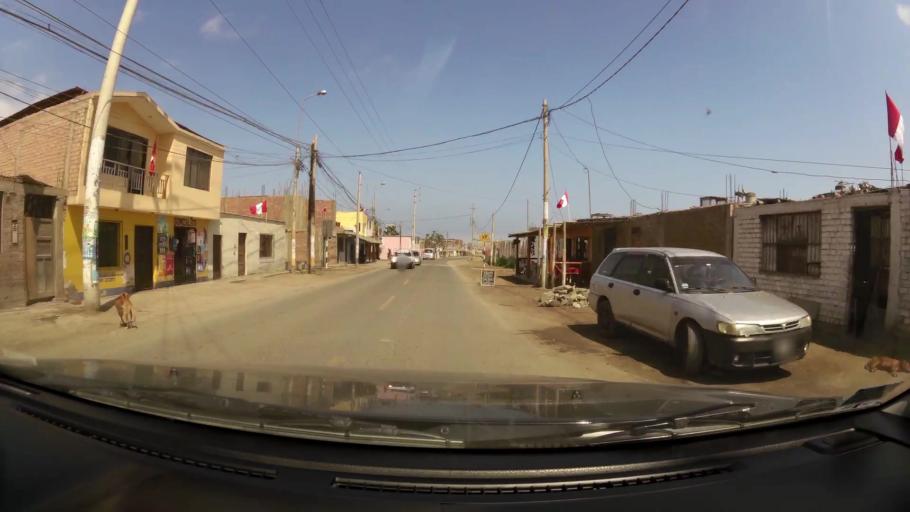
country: PE
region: Lima
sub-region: Provincia de Canete
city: Mala
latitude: -12.6682
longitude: -76.6425
